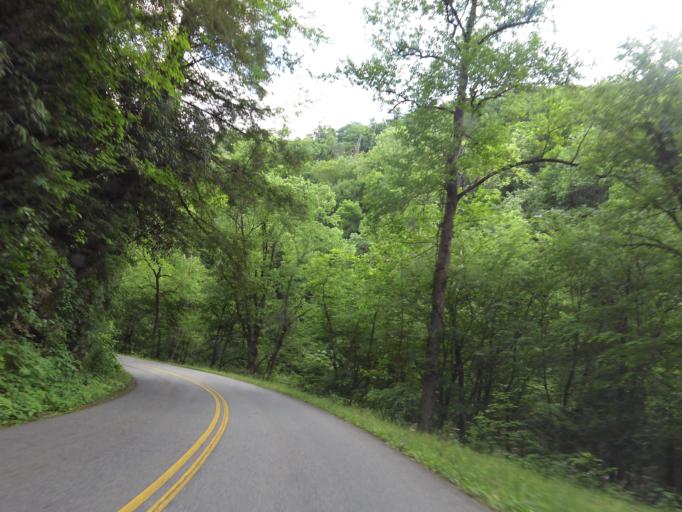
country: US
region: Tennessee
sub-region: Sevier County
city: Pigeon Forge
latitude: 35.6684
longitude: -83.6996
